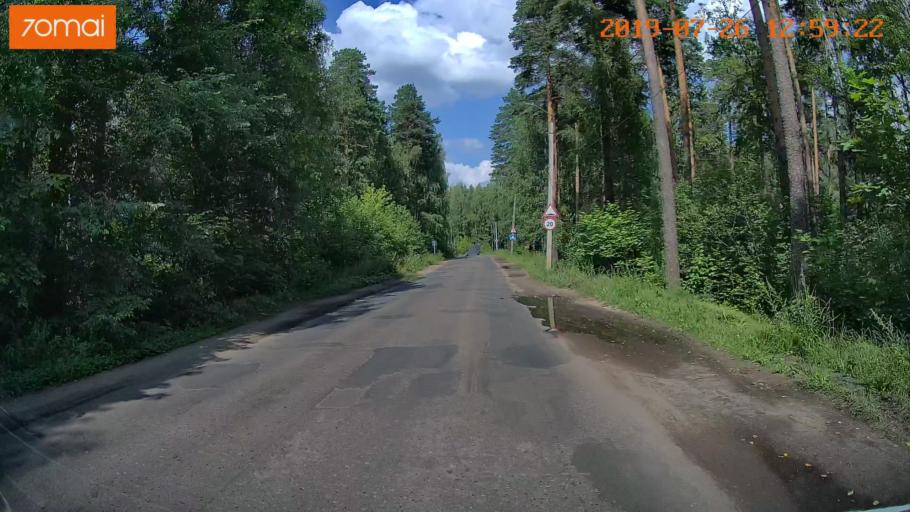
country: RU
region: Ivanovo
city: Bogorodskoye
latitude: 57.0285
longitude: 41.0209
